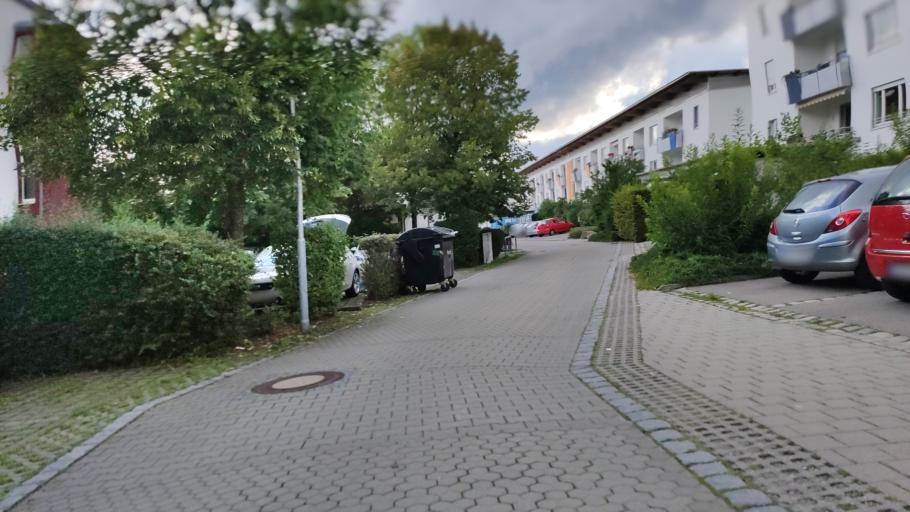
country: DE
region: Bavaria
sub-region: Swabia
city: Konigsbrunn
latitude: 48.2582
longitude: 10.8905
